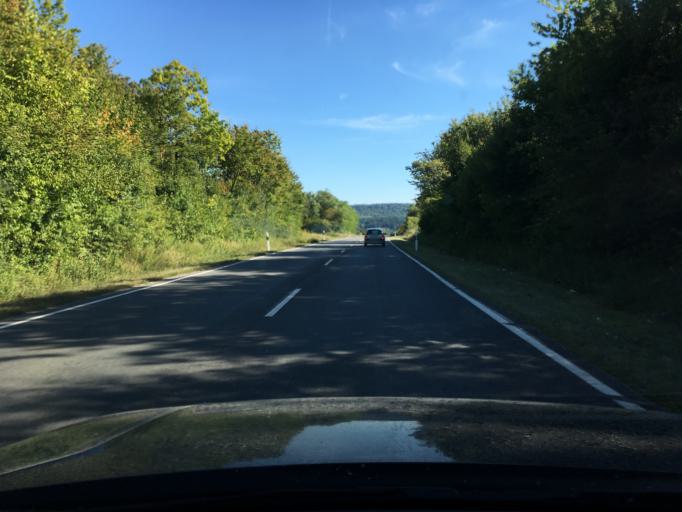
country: DE
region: Baden-Wuerttemberg
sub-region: Regierungsbezirk Stuttgart
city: Gemmingen
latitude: 49.1386
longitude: 8.9968
